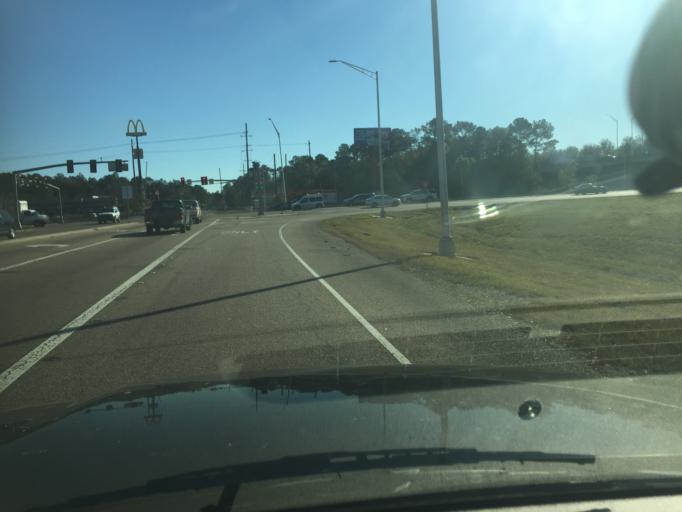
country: US
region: Louisiana
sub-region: Saint Tammany Parish
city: Slidell
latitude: 30.3119
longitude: -89.7710
